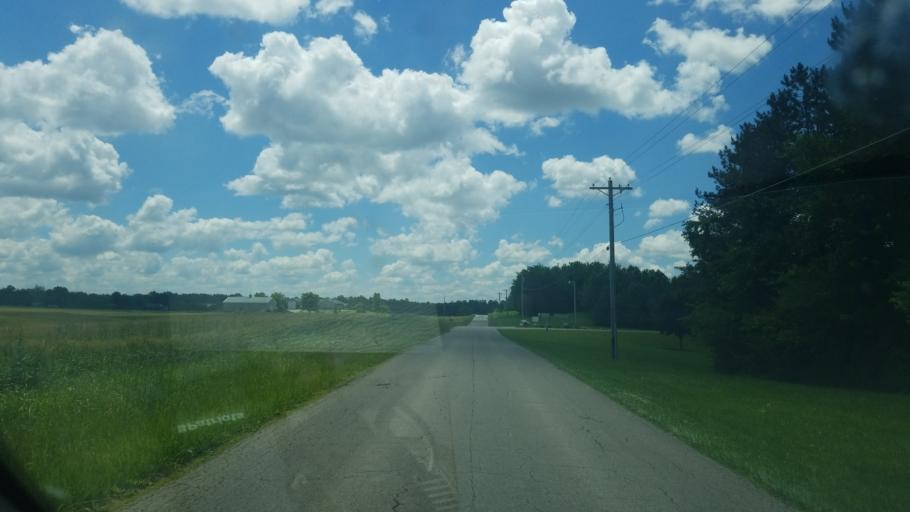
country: US
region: Ohio
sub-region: Huron County
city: New London
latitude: 41.0716
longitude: -82.4173
